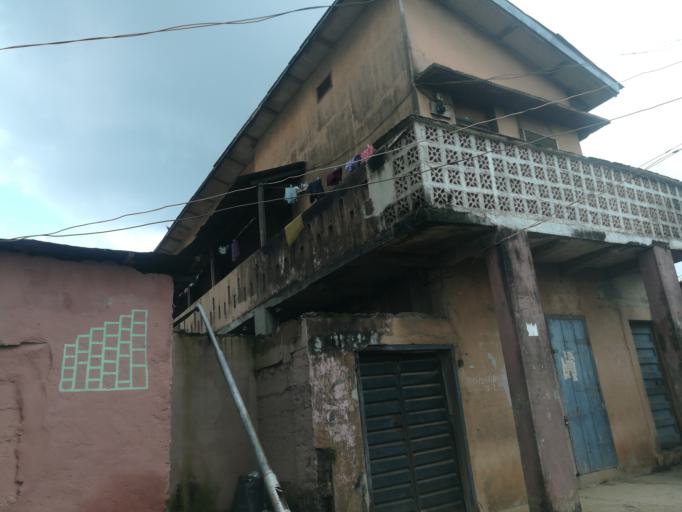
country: NG
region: Lagos
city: Mushin
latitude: 6.5298
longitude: 3.3637
